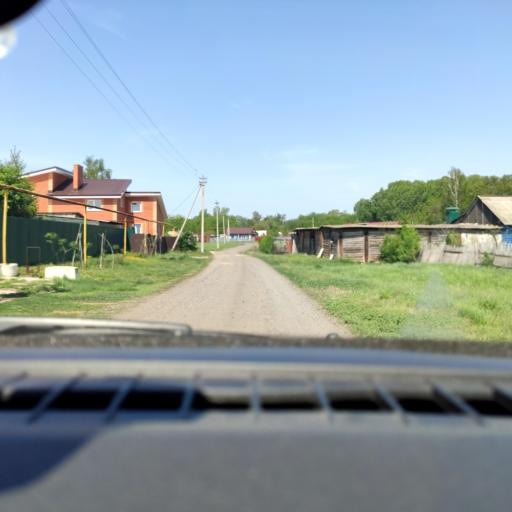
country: RU
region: Samara
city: Georgiyevka
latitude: 53.2771
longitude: 50.9639
